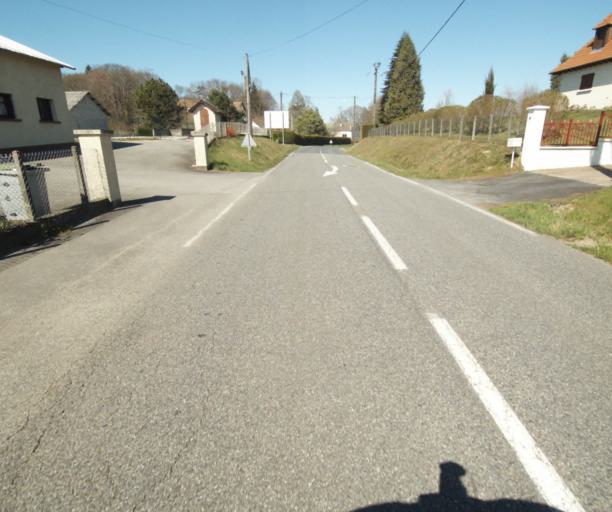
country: FR
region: Limousin
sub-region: Departement de la Correze
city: Saint-Mexant
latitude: 45.2729
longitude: 1.6659
